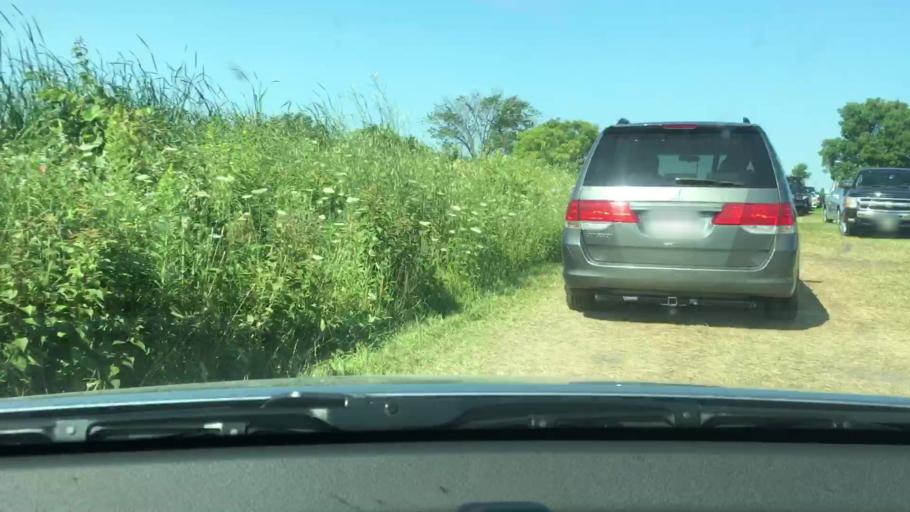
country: US
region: Wisconsin
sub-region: Winnebago County
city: Oshkosh
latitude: 43.9809
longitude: -88.5780
